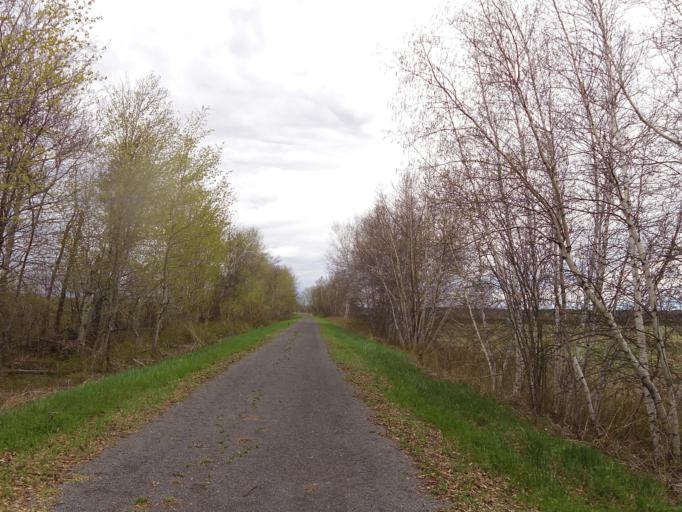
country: CA
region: Quebec
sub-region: Outaouais
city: Papineauville
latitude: 45.5402
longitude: -74.8592
